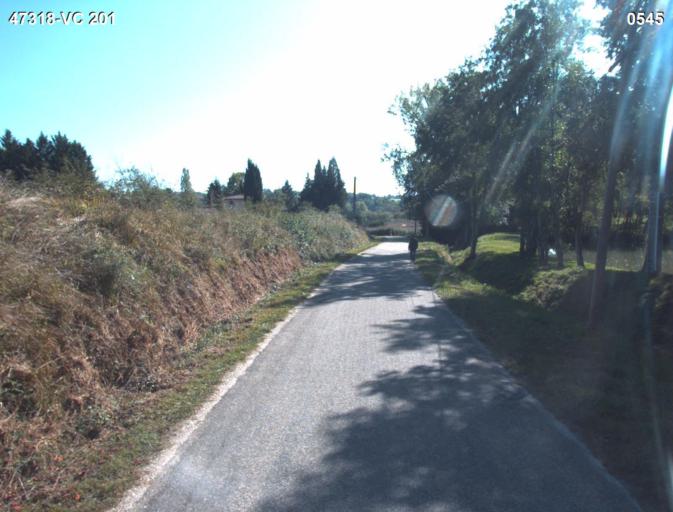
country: FR
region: Aquitaine
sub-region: Departement du Lot-et-Garonne
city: Vianne
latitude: 44.2026
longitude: 0.3191
